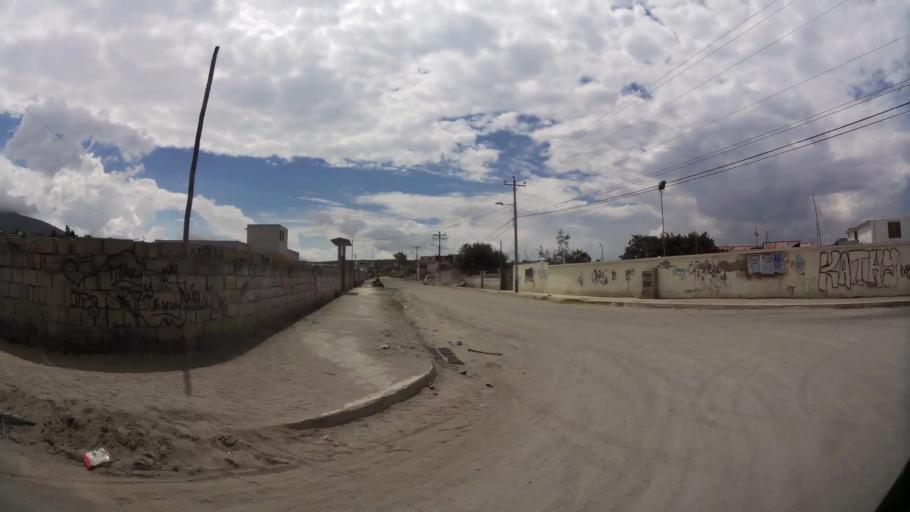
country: EC
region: Pichincha
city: Quito
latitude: -0.0635
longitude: -78.4260
